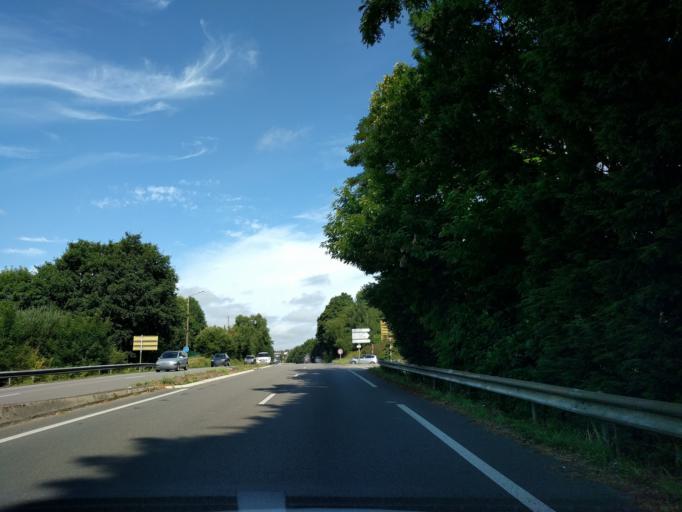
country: FR
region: Brittany
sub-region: Departement du Finistere
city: Quimper
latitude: 48.0014
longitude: -4.0782
